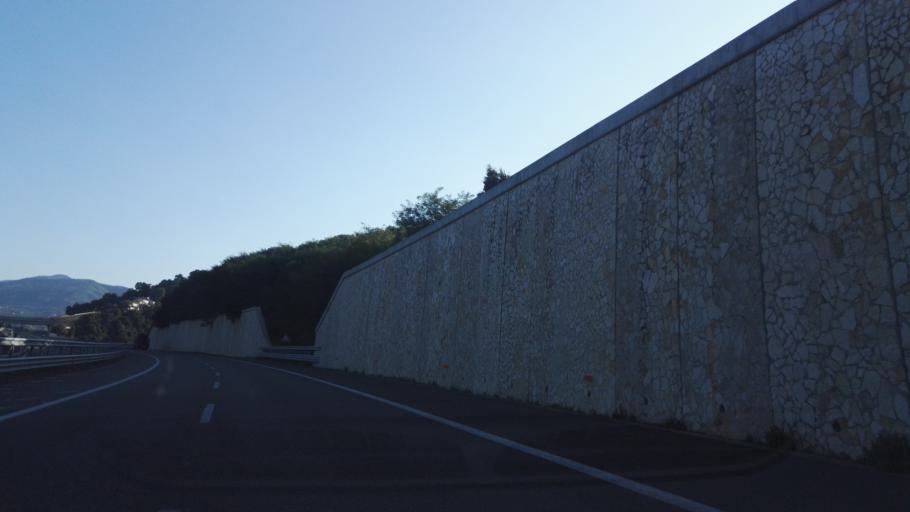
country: IT
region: Calabria
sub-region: Provincia di Catanzaro
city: Nocera Scalo
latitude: 39.0321
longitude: 16.1333
